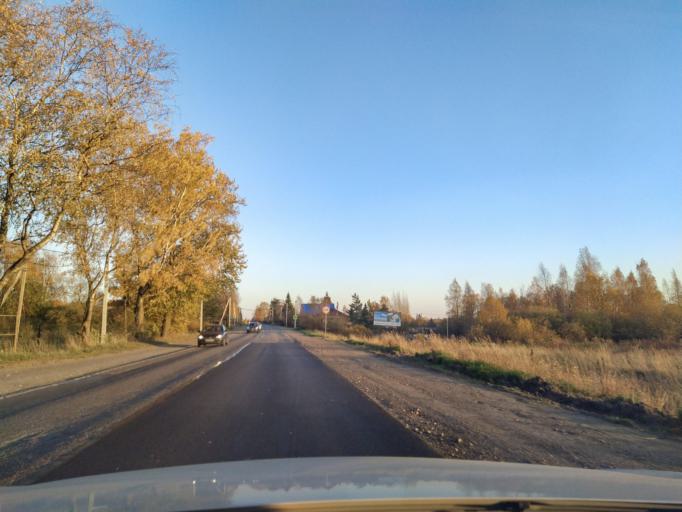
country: RU
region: Leningrad
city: Maloye Verevo
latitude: 59.6150
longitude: 30.2177
